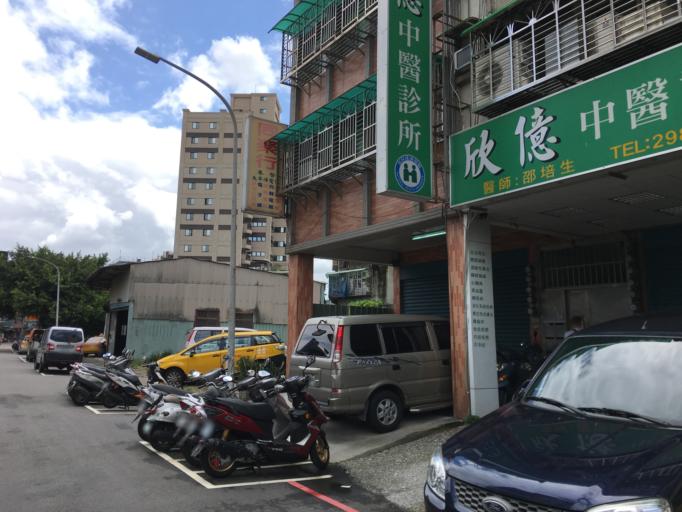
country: TW
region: Taipei
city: Taipei
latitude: 25.0819
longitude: 121.4897
